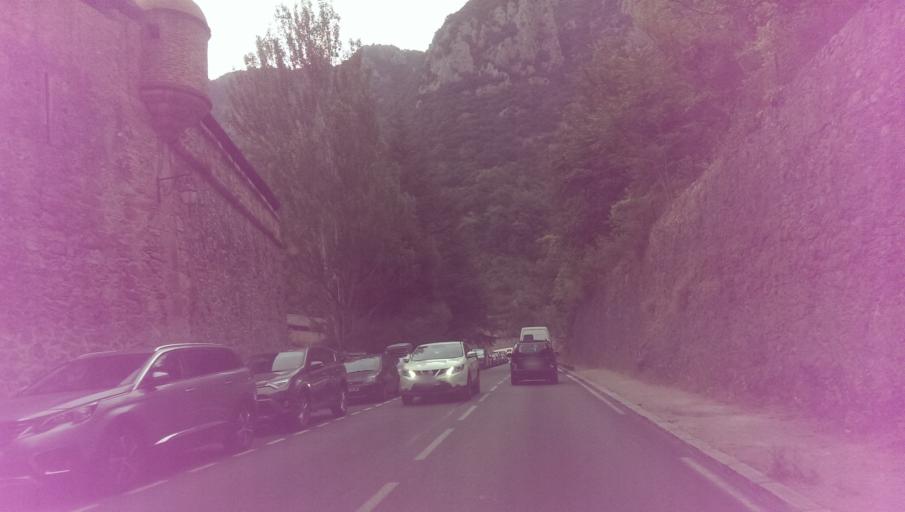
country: FR
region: Languedoc-Roussillon
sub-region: Departement des Pyrenees-Orientales
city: Vernet-les-Bains
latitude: 42.5864
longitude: 2.3680
